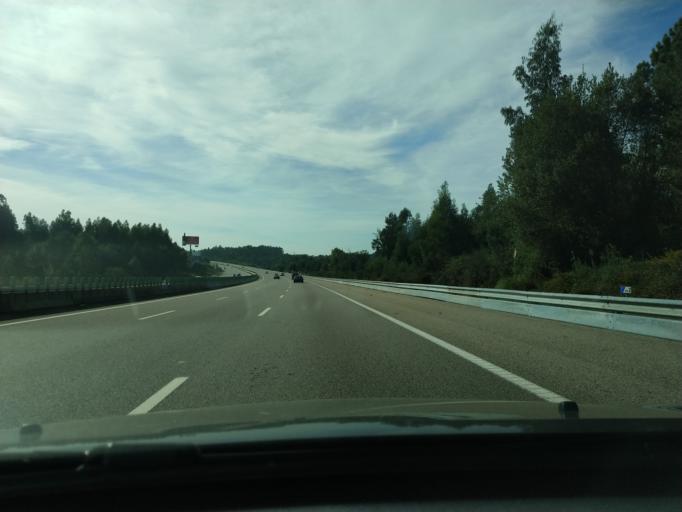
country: PT
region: Aveiro
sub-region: Santa Maria da Feira
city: Feira
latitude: 40.8965
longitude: -8.5683
